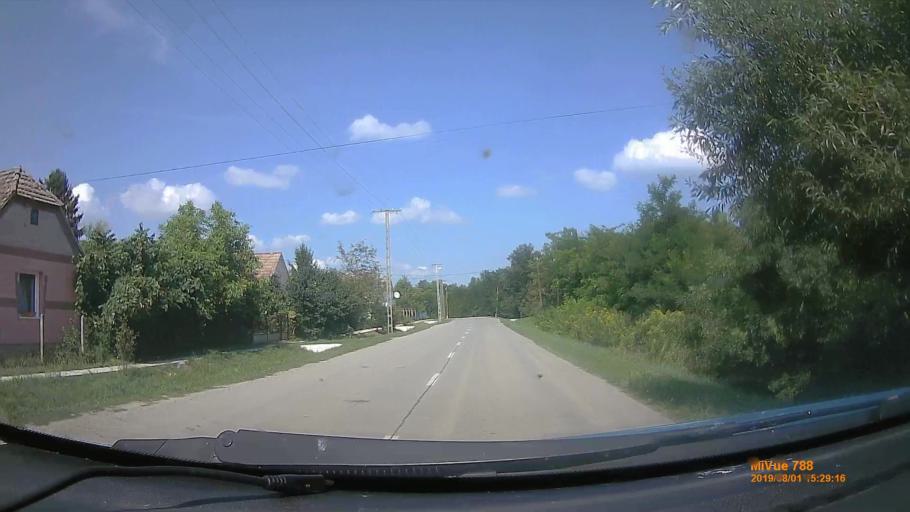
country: HU
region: Baranya
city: Sellye
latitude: 45.9225
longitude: 17.8708
